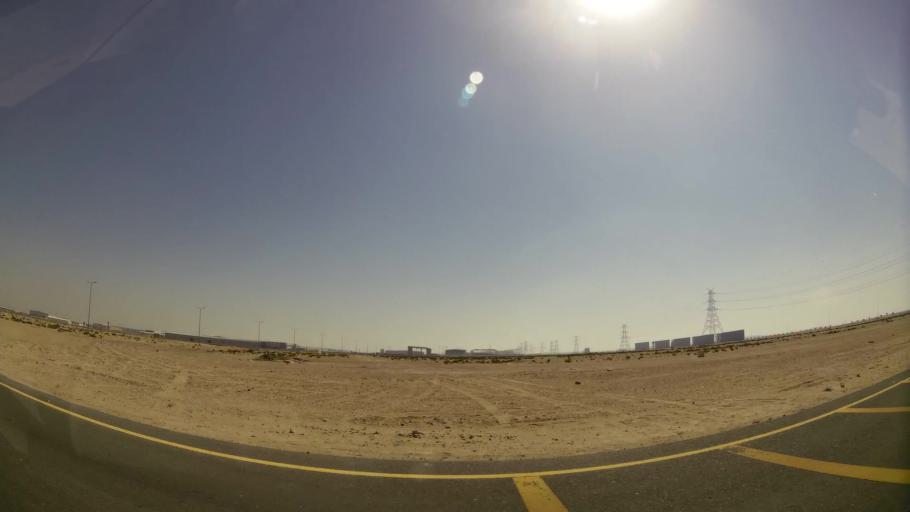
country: AE
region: Dubai
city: Dubai
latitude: 24.9028
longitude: 55.0660
